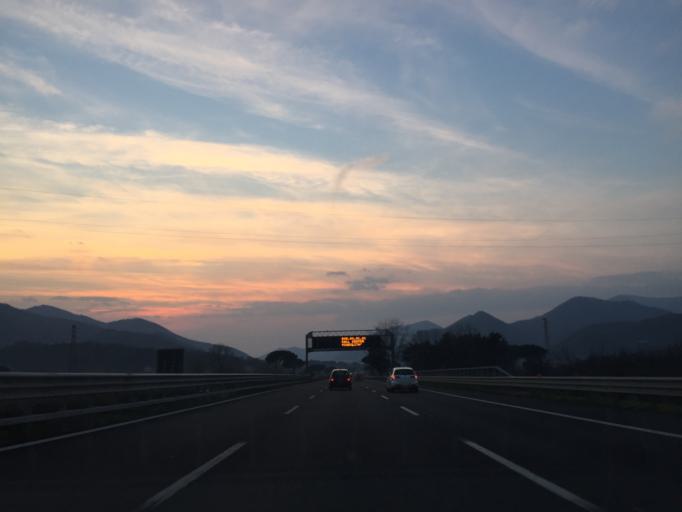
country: IT
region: Campania
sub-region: Provincia di Salerno
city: Faraldo-Nocelleto
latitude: 40.7726
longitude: 14.7744
